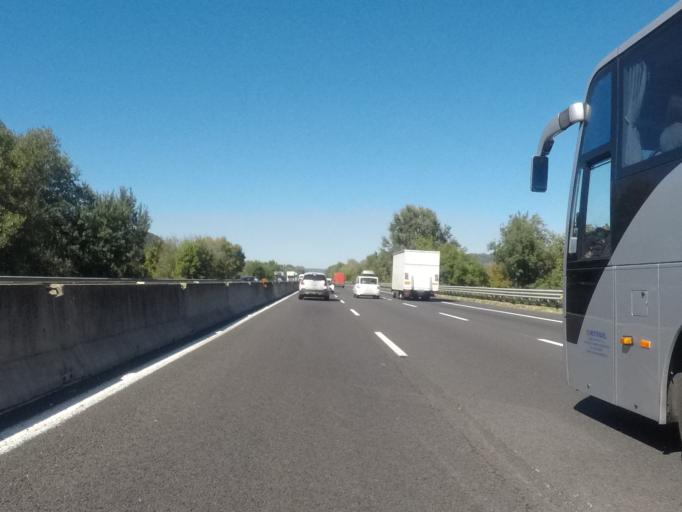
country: IT
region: Umbria
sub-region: Provincia di Terni
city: Otricoli
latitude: 42.4036
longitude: 12.4545
